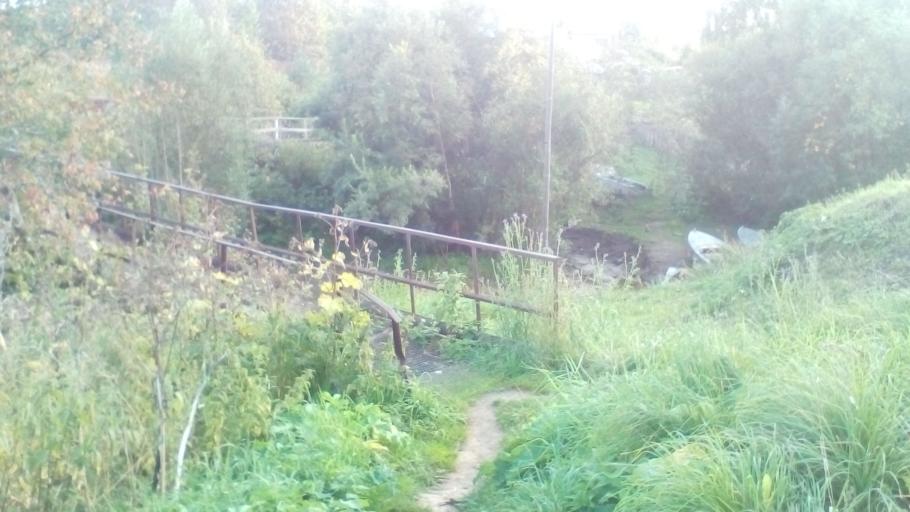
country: RU
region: Perm
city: Usol'ye
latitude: 59.4844
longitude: 56.5847
